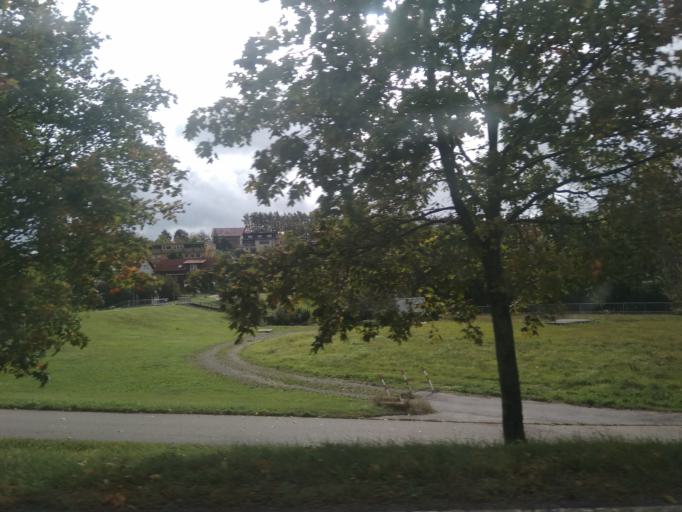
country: DE
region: Baden-Wuerttemberg
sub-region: Karlsruhe Region
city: Seckach
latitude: 49.4082
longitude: 9.2798
